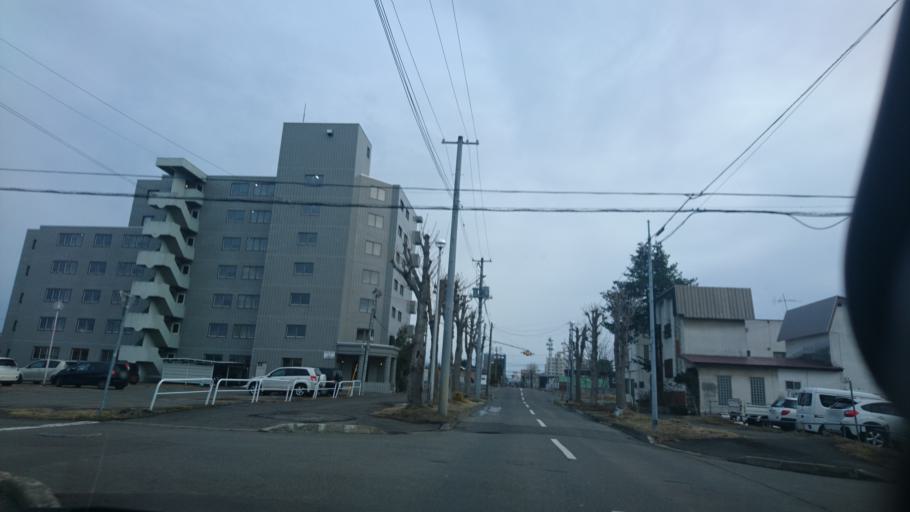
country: JP
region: Hokkaido
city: Obihiro
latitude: 42.9300
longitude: 143.1978
